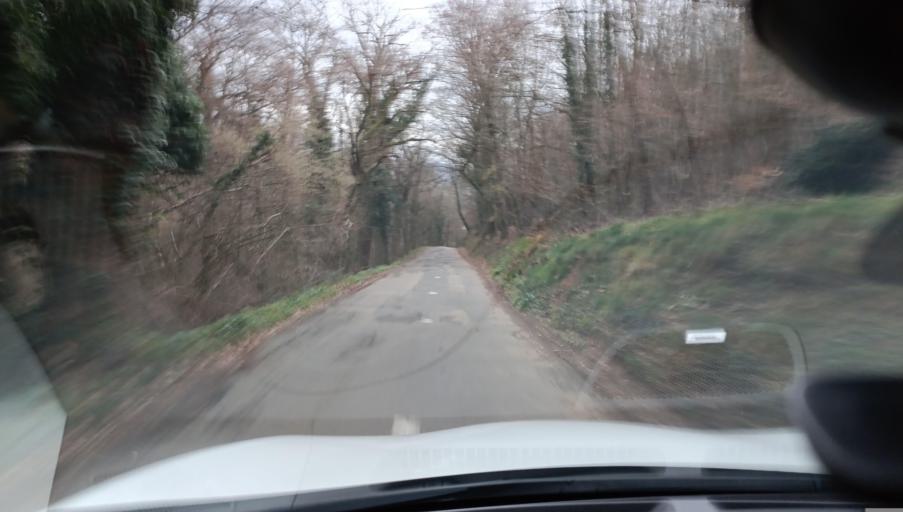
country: FR
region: Rhone-Alpes
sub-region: Departement de l'Isere
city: Chasse-sur-Rhone
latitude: 45.5758
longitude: 4.8213
